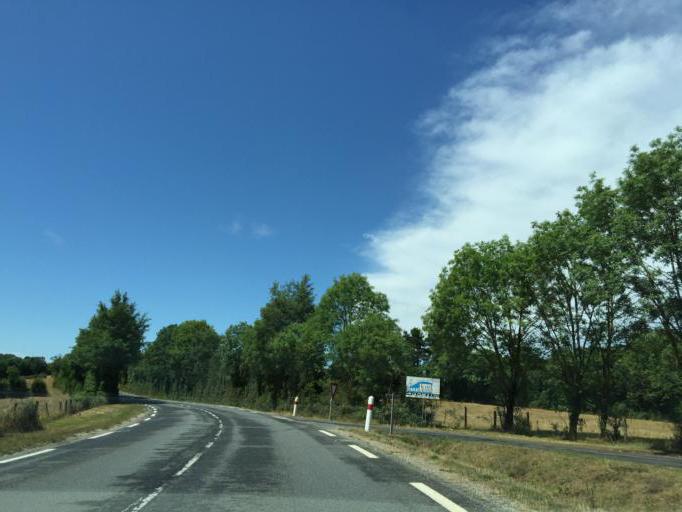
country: FR
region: Midi-Pyrenees
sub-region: Departement de l'Aveyron
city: Severac-le-Chateau
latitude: 44.2253
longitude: 2.9929
